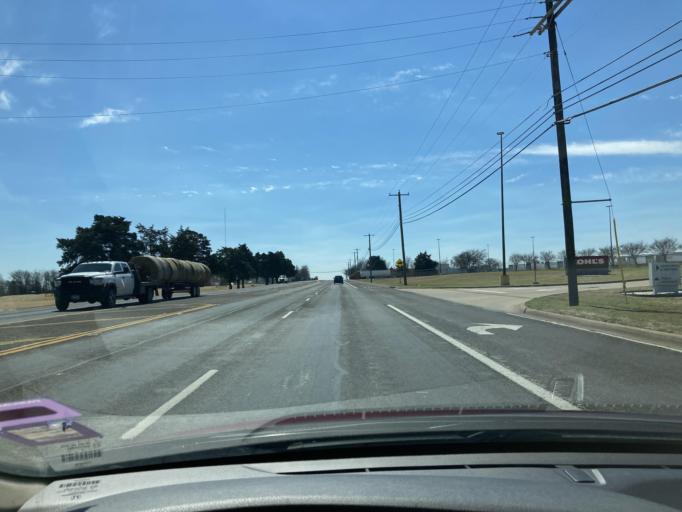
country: US
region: Texas
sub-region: Navarro County
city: Corsicana
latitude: 32.1176
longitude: -96.4650
